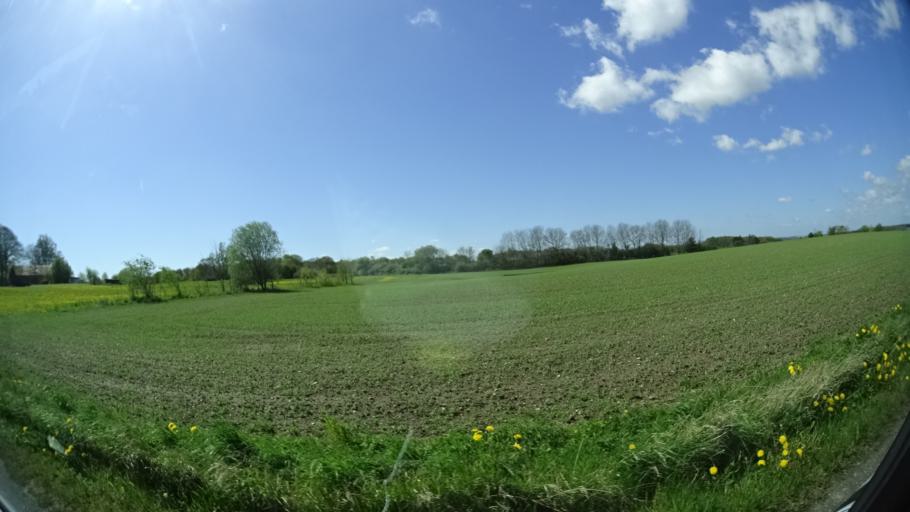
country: DK
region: Central Jutland
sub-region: Skanderborg Kommune
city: Horning
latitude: 56.1185
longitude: 10.0188
